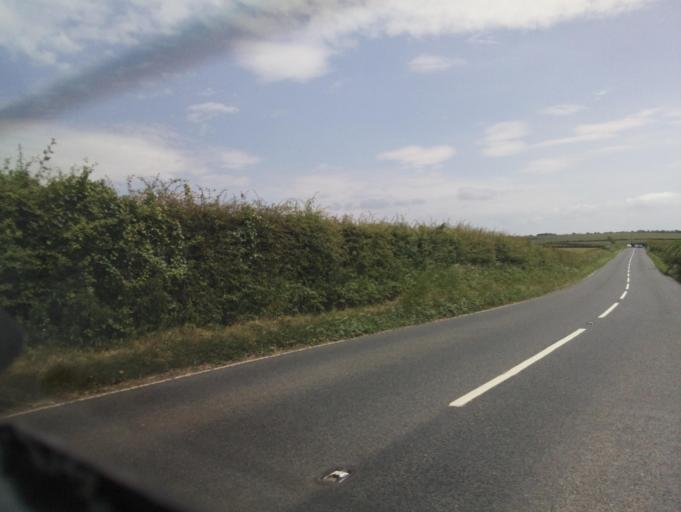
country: GB
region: Wales
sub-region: Vale of Glamorgan
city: Wick
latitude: 51.4469
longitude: -3.5732
